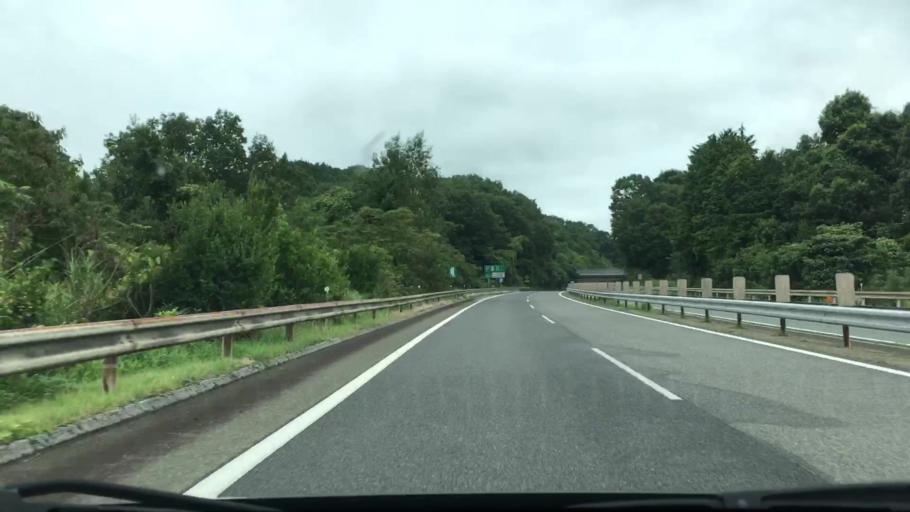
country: JP
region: Hiroshima
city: Shobara
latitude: 34.8372
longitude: 132.9824
